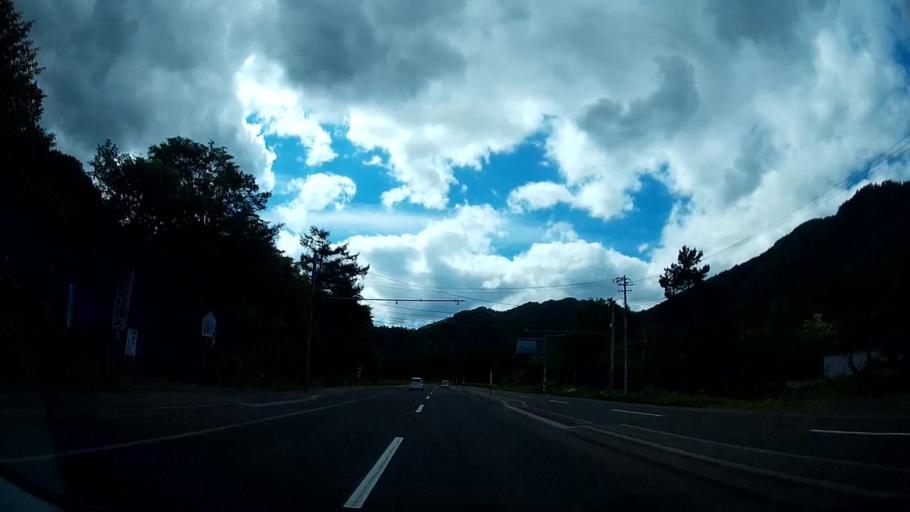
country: JP
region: Hokkaido
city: Sapporo
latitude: 42.9690
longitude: 141.1927
